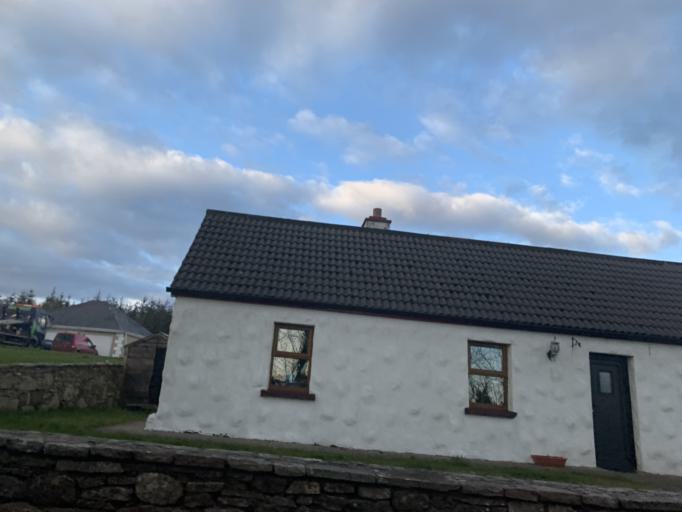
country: IE
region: Connaught
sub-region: Maigh Eo
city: Ballyhaunis
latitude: 53.8653
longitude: -8.7610
